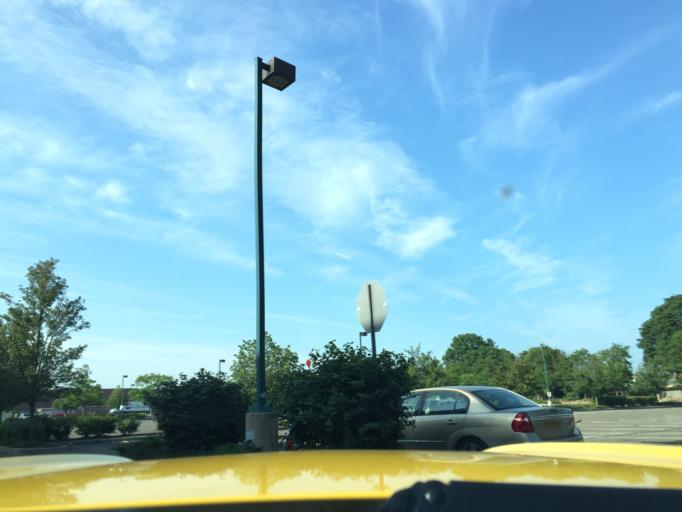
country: US
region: New York
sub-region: Nassau County
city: Hicksville
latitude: 40.7745
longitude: -73.5337
